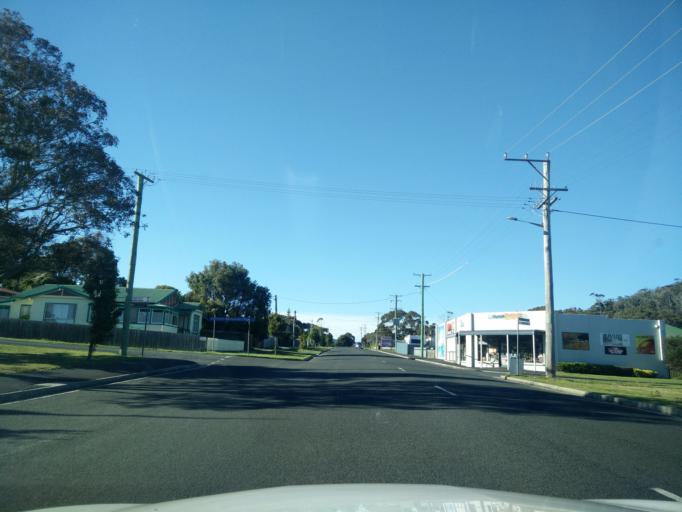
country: AU
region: Tasmania
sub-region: Break O'Day
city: St Helens
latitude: -41.8764
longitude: 148.3039
